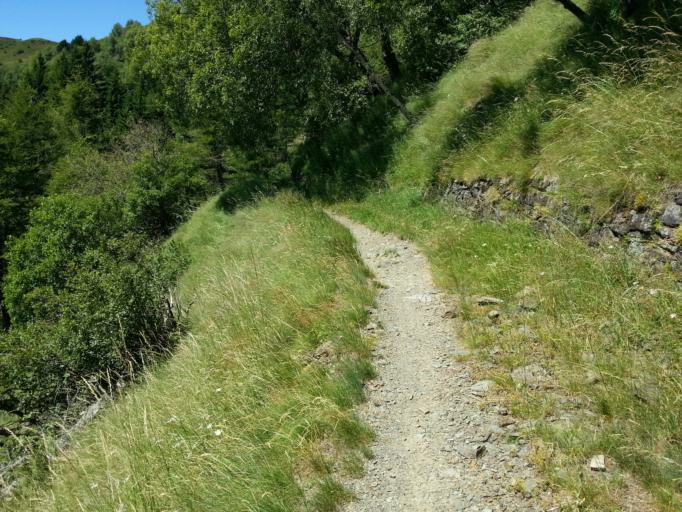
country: CH
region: Ticino
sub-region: Bellinzona District
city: Camorino
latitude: 46.1092
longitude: 9.0335
